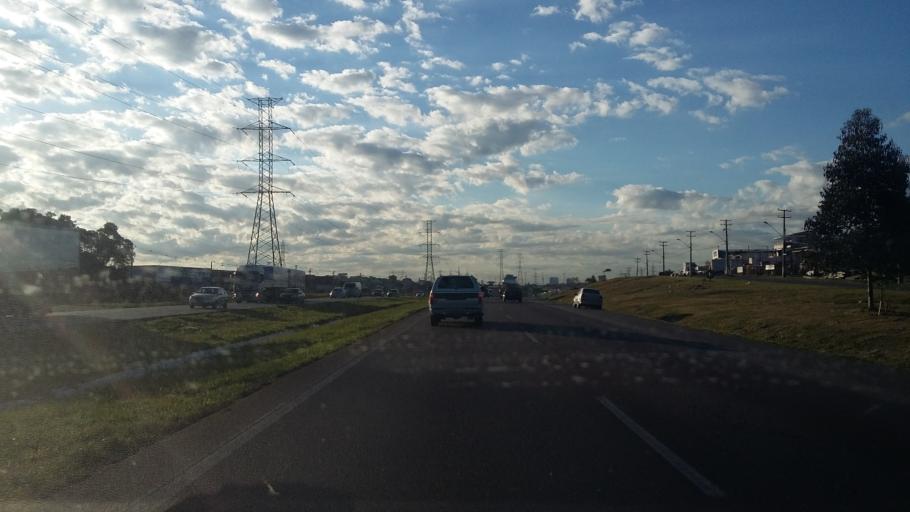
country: BR
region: Parana
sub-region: Curitiba
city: Curitiba
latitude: -25.5082
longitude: -49.3400
